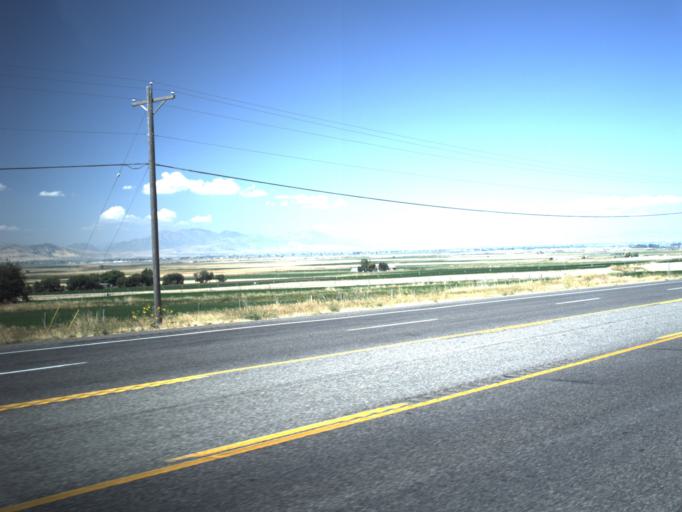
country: US
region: Utah
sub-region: Cache County
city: Smithfield
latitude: 41.8661
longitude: -111.8290
